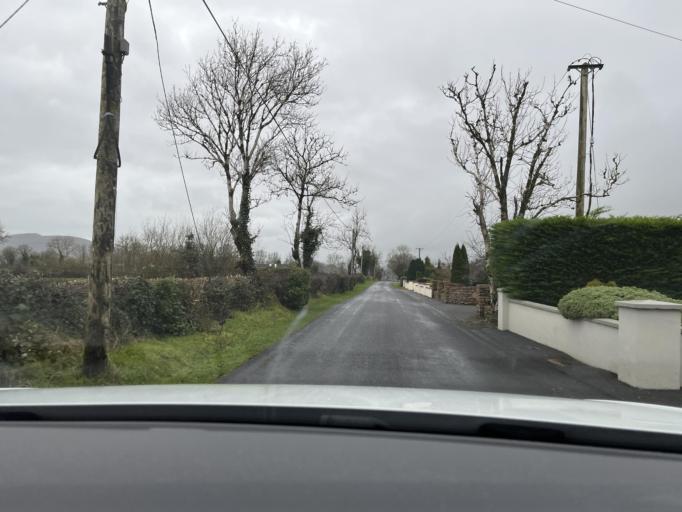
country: IE
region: Connaught
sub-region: County Leitrim
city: Manorhamilton
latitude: 54.2991
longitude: -8.1481
